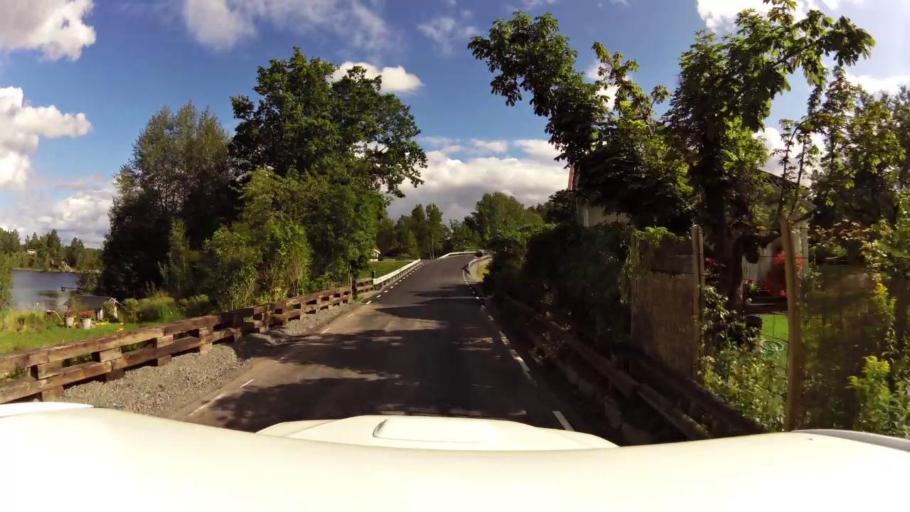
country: SE
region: OEstergoetland
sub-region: Kinda Kommun
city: Rimforsa
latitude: 58.2285
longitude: 15.7005
